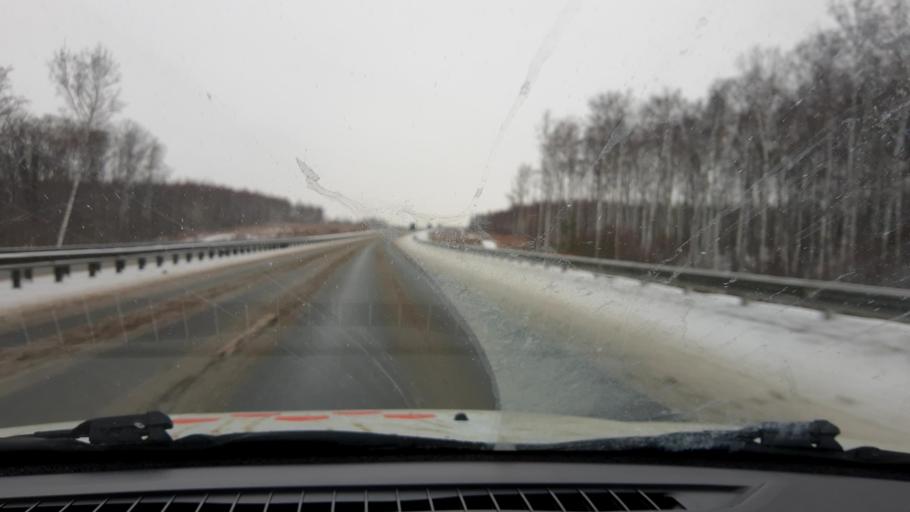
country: RU
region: Nizjnij Novgorod
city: Afonino
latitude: 56.1076
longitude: 43.9870
